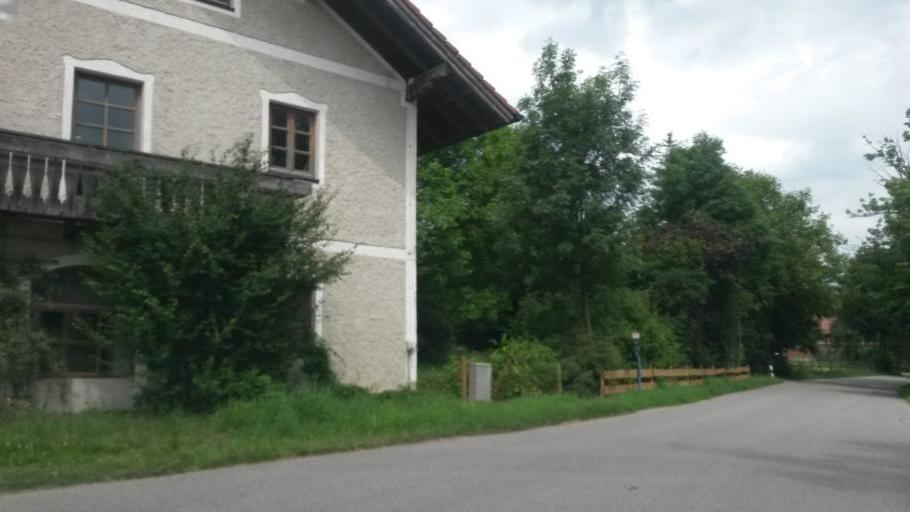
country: DE
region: Bavaria
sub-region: Upper Bavaria
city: Hoslwang
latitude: 47.9452
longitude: 12.3404
